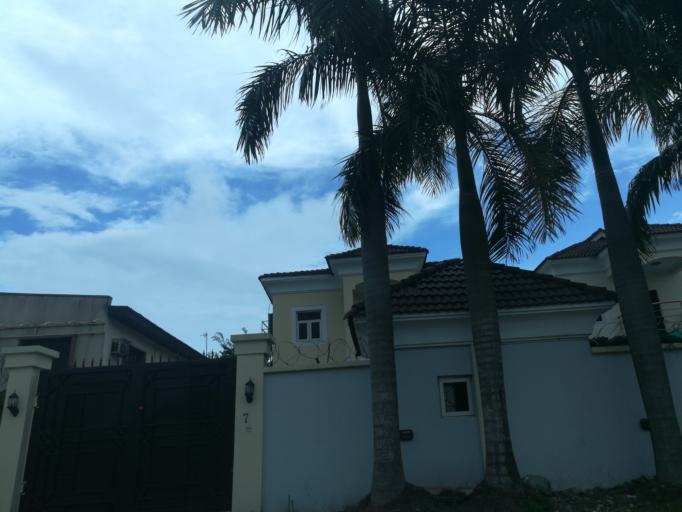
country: NG
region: Lagos
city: Ikoyi
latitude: 6.4435
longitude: 3.4751
